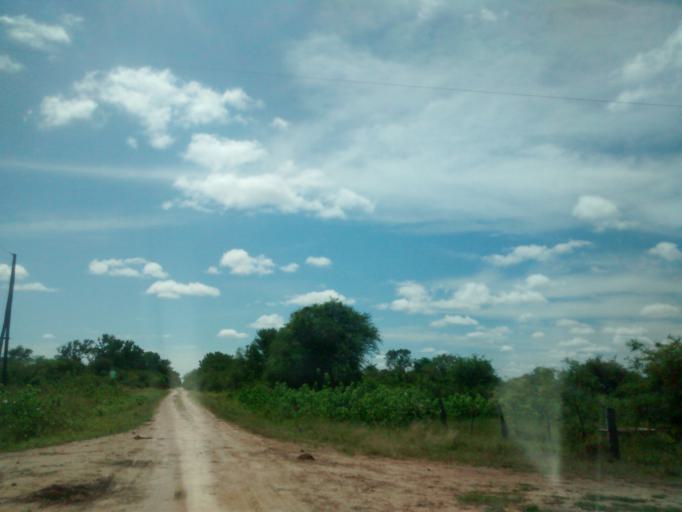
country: AR
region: Chaco
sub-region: Departamento de Quitilipi
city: Quitilipi
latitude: -26.7738
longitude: -60.2506
